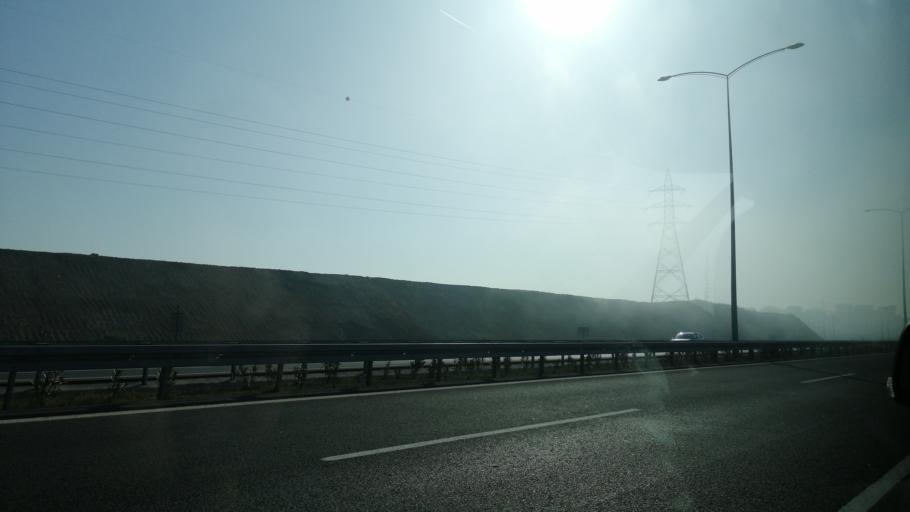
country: TR
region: Kocaeli
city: Tavsanli
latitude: 40.7890
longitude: 29.5143
